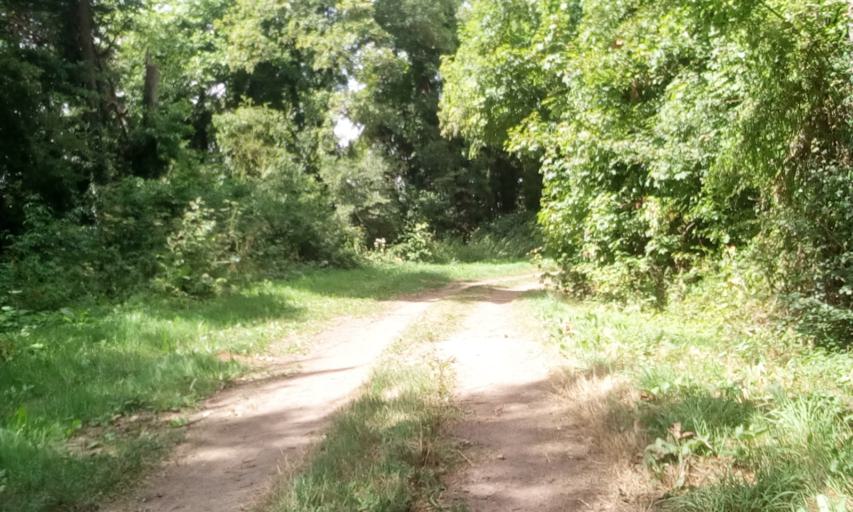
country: FR
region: Lower Normandy
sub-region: Departement du Calvados
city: Sannerville
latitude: 49.1606
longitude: -0.2145
